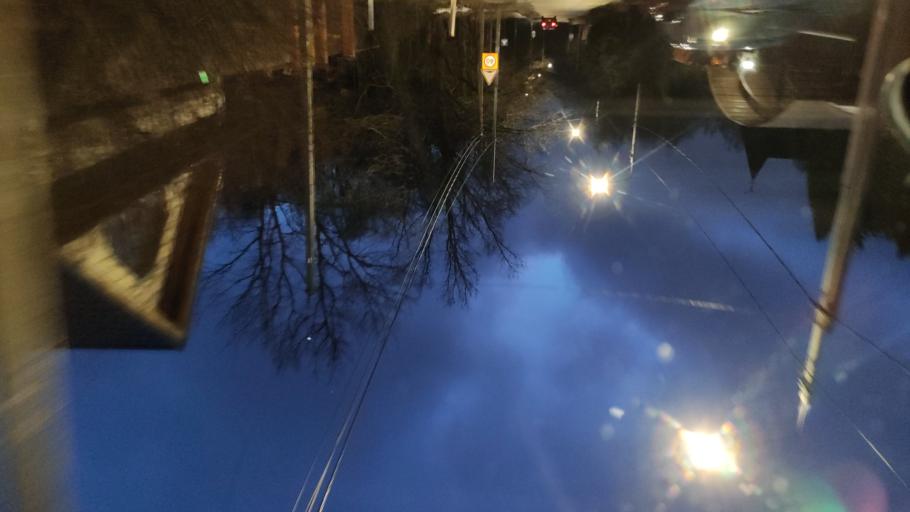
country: RU
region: Moskovskaya
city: Biryulevo Zapadnoye
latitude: 55.5536
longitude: 37.6275
